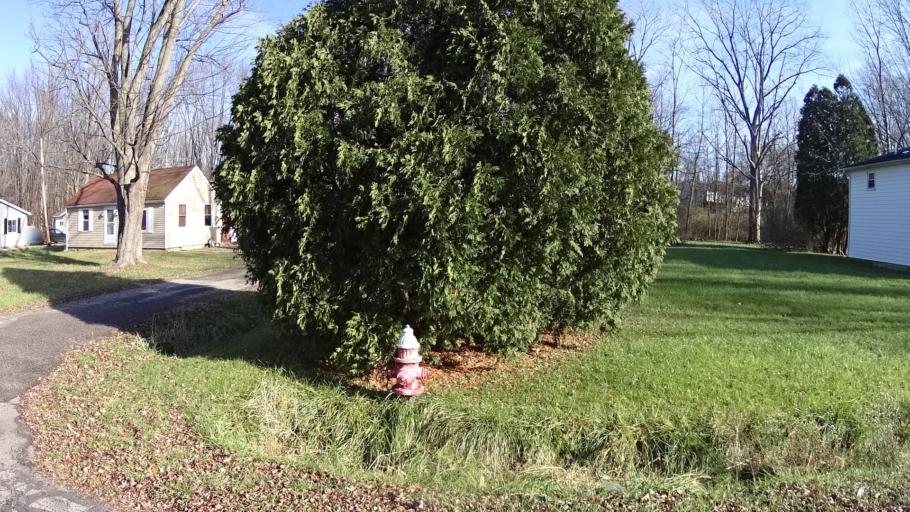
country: US
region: Ohio
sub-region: Lorain County
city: North Ridgeville
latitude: 41.4045
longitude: -81.9870
